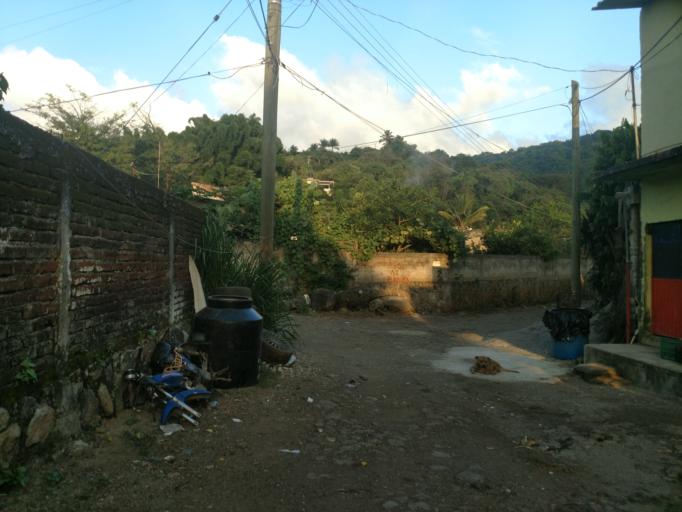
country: MX
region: Nayarit
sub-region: Tepic
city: La Corregidora
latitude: 21.4646
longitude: -104.7995
